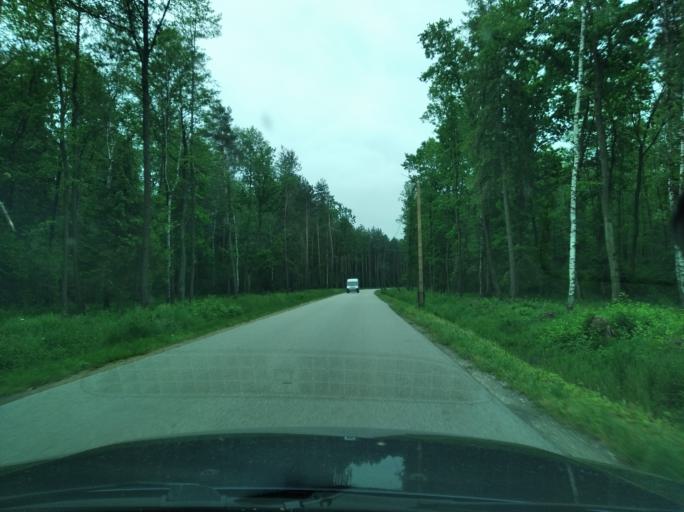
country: PL
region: Subcarpathian Voivodeship
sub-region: Powiat ropczycko-sedziszowski
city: Sedziszow Malopolski
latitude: 50.1310
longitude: 21.6708
